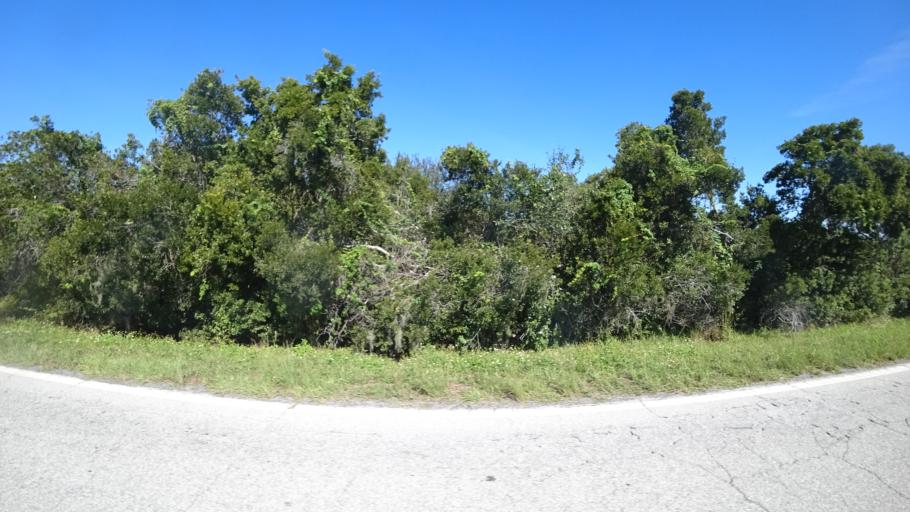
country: US
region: Florida
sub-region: Hillsborough County
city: Wimauma
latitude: 27.5373
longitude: -82.0873
